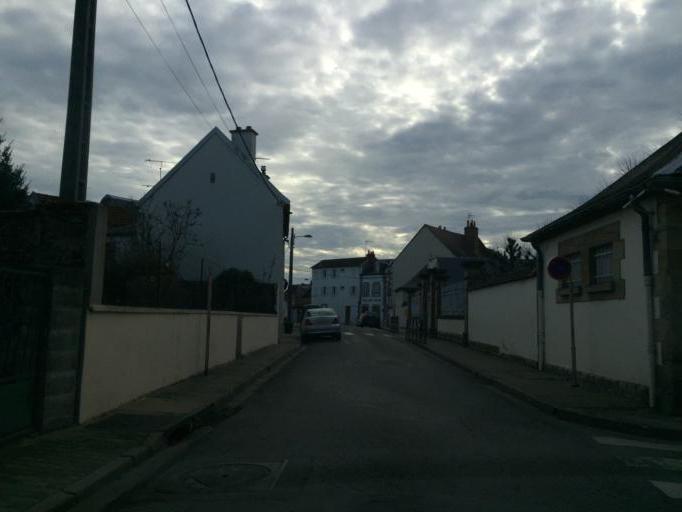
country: FR
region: Auvergne
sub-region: Departement de l'Allier
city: Moulins
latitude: 46.5698
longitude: 3.3377
